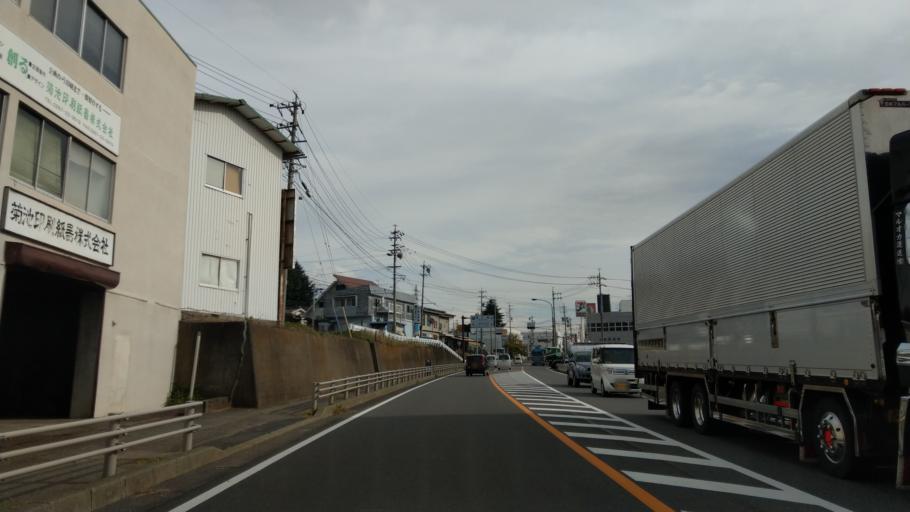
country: JP
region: Nagano
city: Komoro
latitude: 36.3309
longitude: 138.4313
